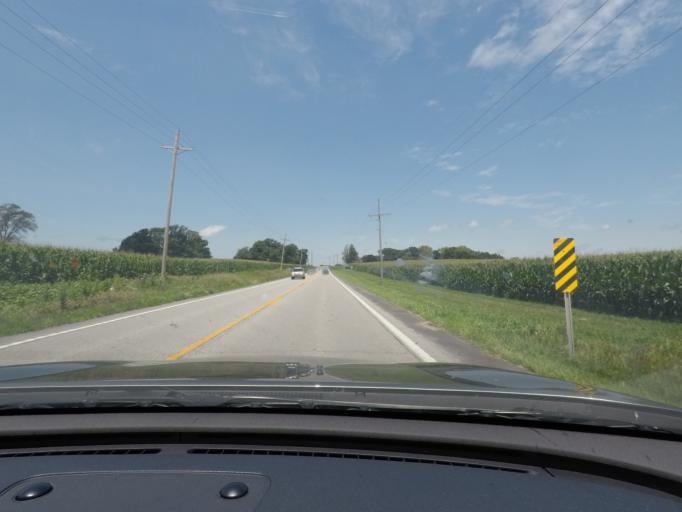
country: US
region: Missouri
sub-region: Saline County
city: Marshall
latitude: 39.1431
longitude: -93.2378
